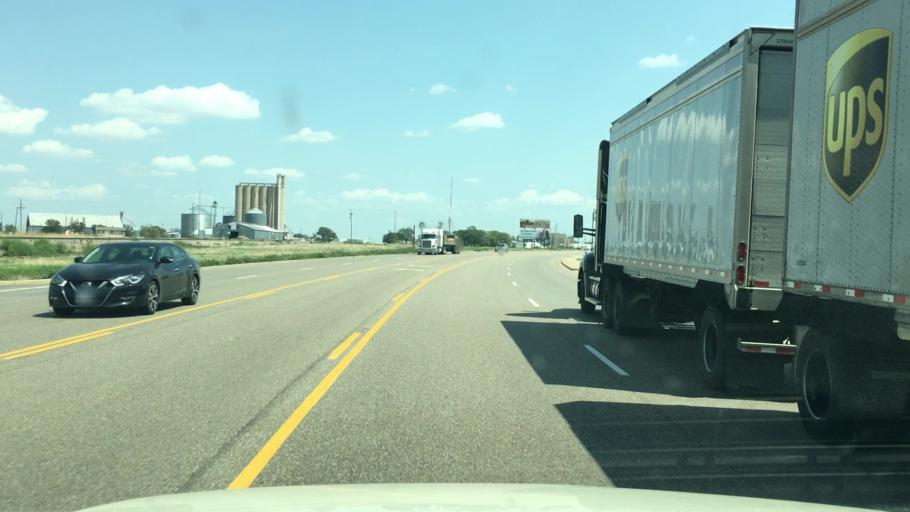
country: US
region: Texas
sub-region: Armstrong County
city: Claude
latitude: 35.1141
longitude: -101.3673
